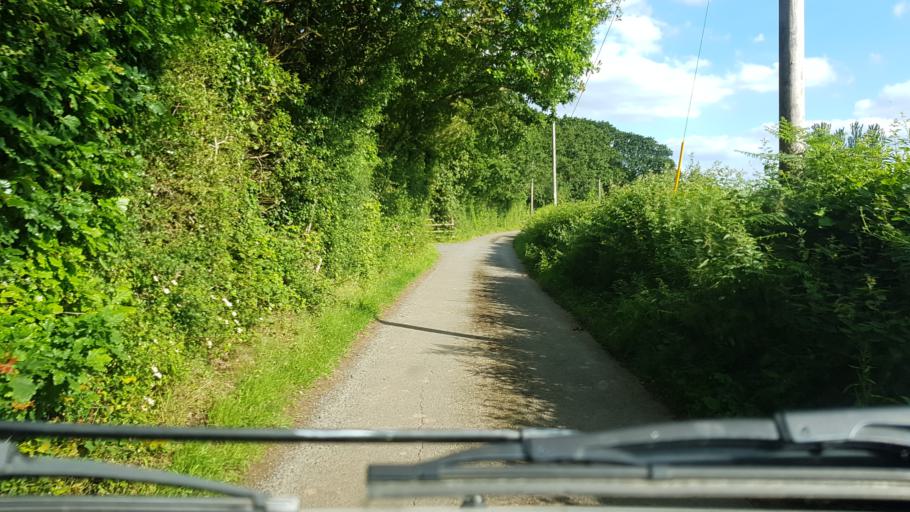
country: GB
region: England
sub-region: Worcestershire
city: Bewdley
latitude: 52.3366
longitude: -2.3208
